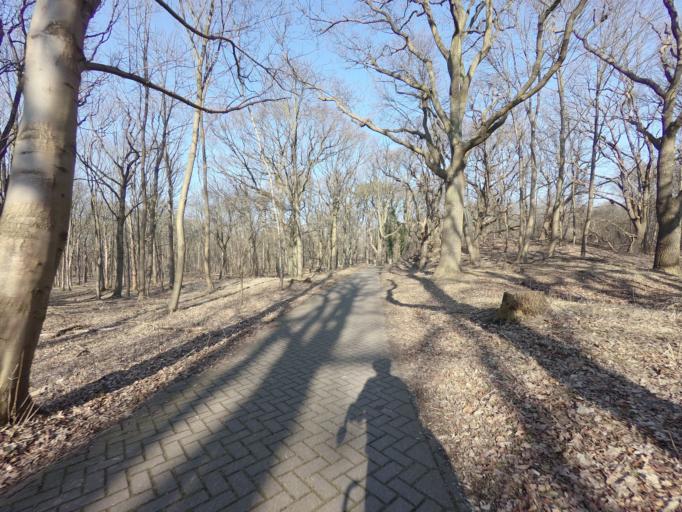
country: NL
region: North Holland
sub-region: Gemeente Bloemendaal
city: Bloemendaal
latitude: 52.4355
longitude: 4.6120
